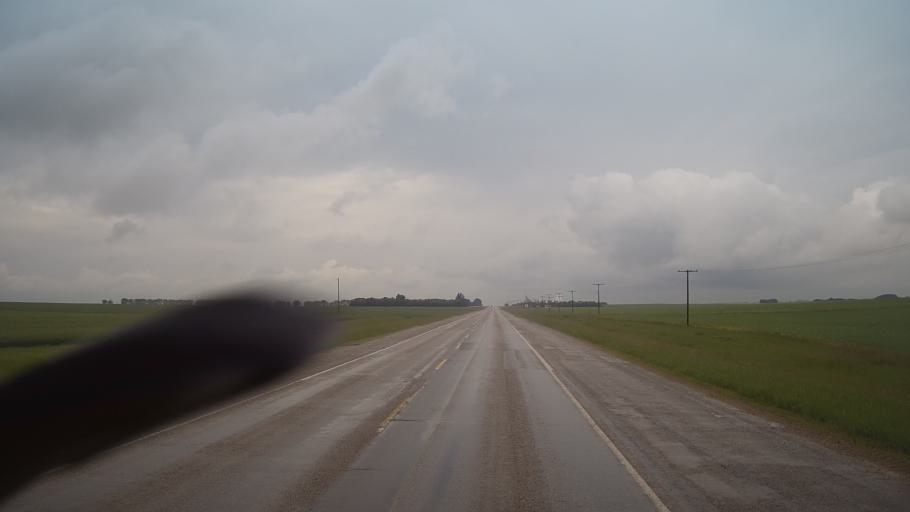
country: CA
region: Saskatchewan
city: Unity
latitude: 52.4349
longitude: -109.0707
